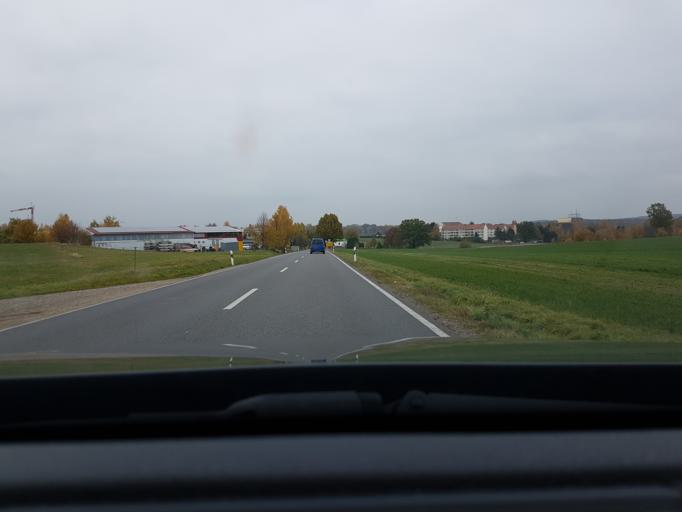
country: DE
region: Saxony
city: Mittweida
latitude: 50.9627
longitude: 12.9778
